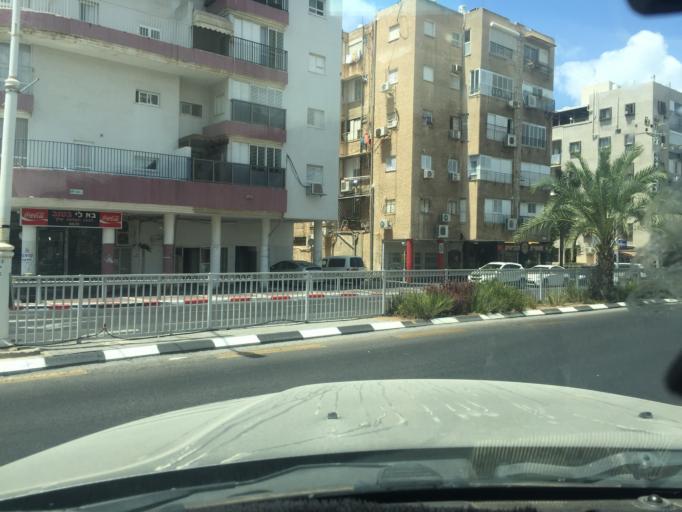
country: IL
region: Tel Aviv
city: Bat Yam
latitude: 32.0112
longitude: 34.7421
